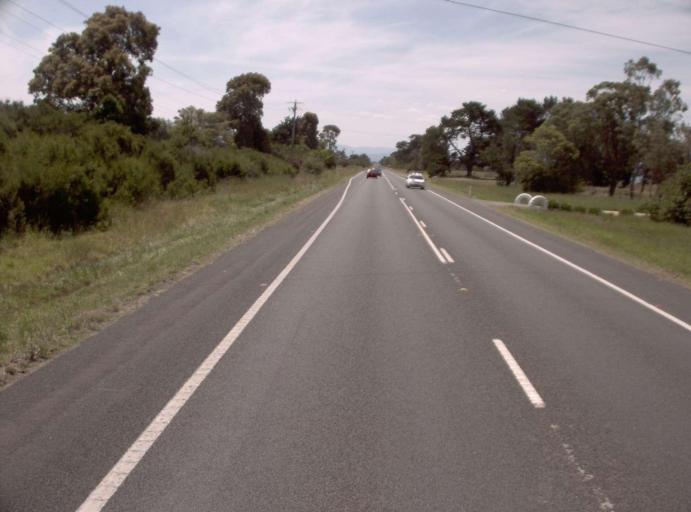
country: AU
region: Victoria
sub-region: Wellington
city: Sale
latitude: -38.0540
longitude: 147.0676
